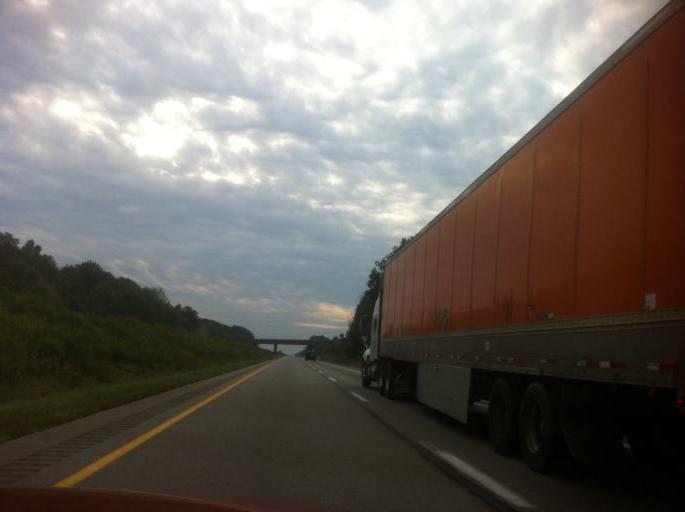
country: US
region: Pennsylvania
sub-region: Mercer County
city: Grove City
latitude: 41.1979
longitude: -79.8968
